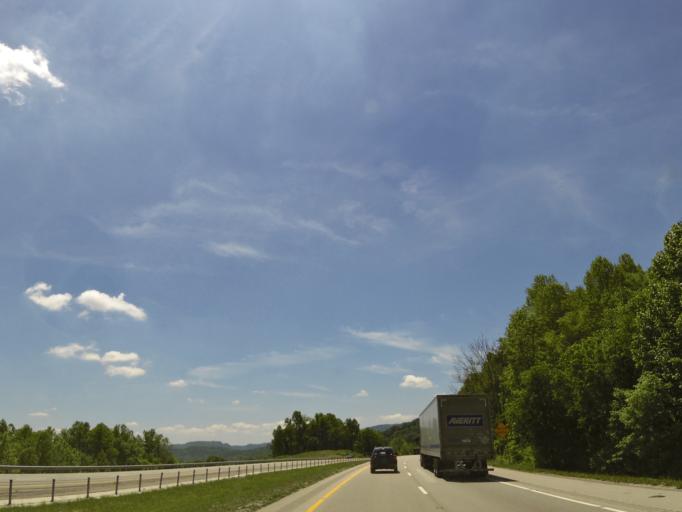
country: US
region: Tennessee
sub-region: Campbell County
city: Jellico
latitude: 36.6386
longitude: -84.1189
